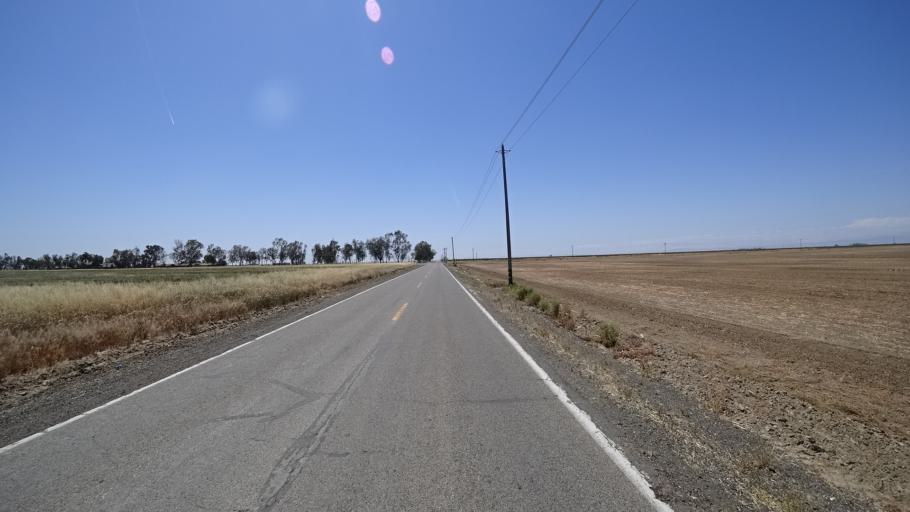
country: US
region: California
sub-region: Kings County
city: Armona
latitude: 36.2135
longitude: -119.7087
